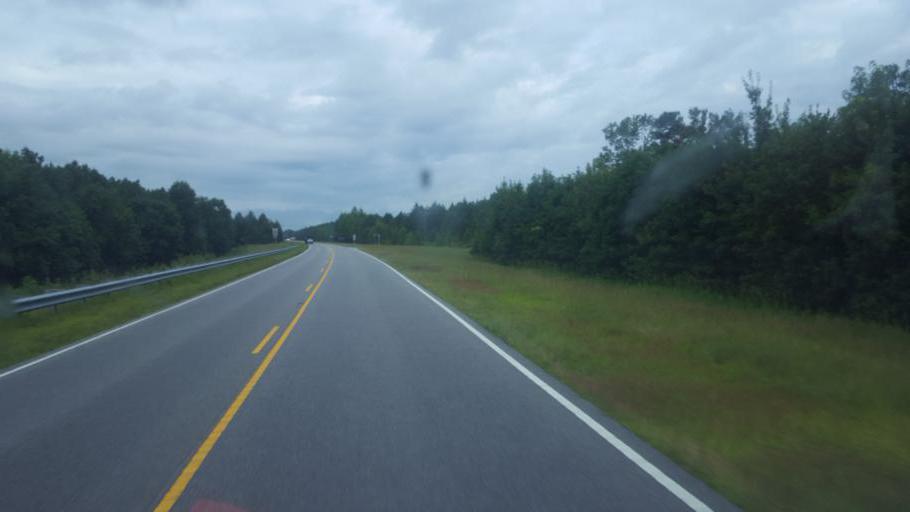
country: US
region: North Carolina
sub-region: Tyrrell County
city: Columbia
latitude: 35.9340
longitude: -76.1616
